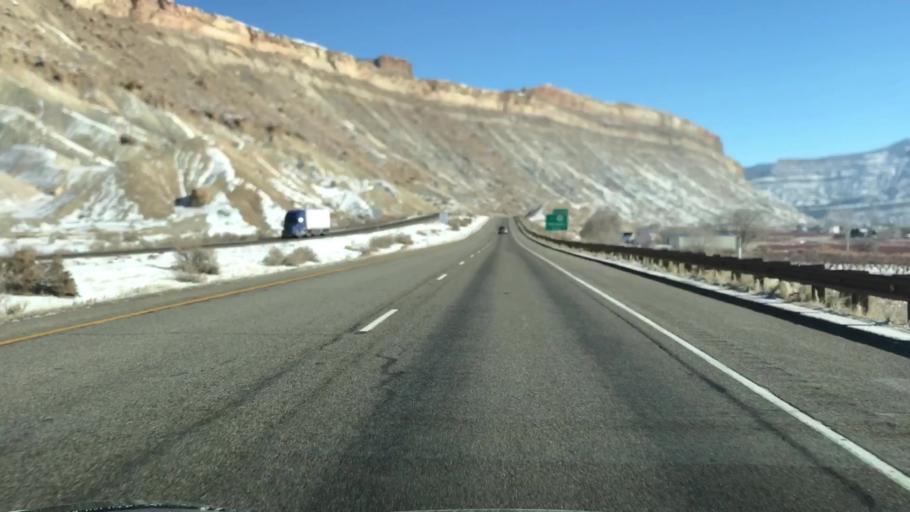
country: US
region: Colorado
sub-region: Mesa County
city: Palisade
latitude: 39.1187
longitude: -108.3836
